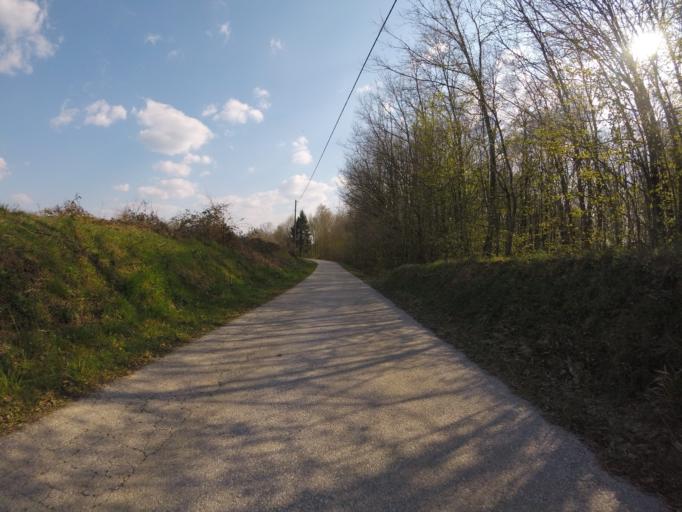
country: HR
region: Sisacko-Moslavacka
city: Glina
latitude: 45.4920
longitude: 16.0008
